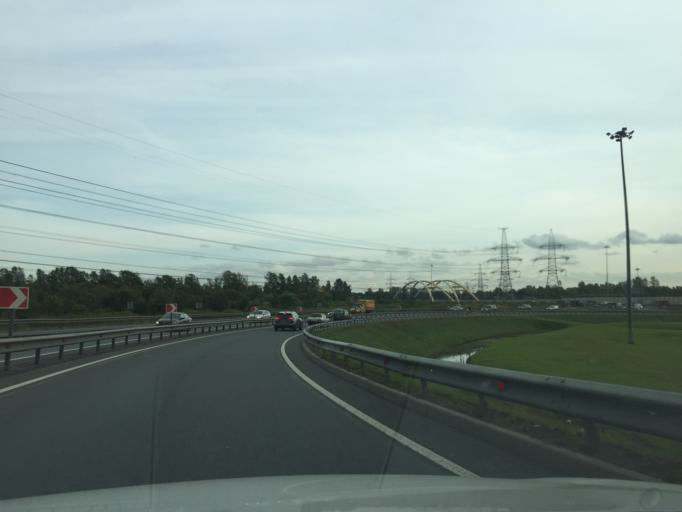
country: RU
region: St.-Petersburg
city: Krasnogvargeisky
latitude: 59.9906
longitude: 30.4867
